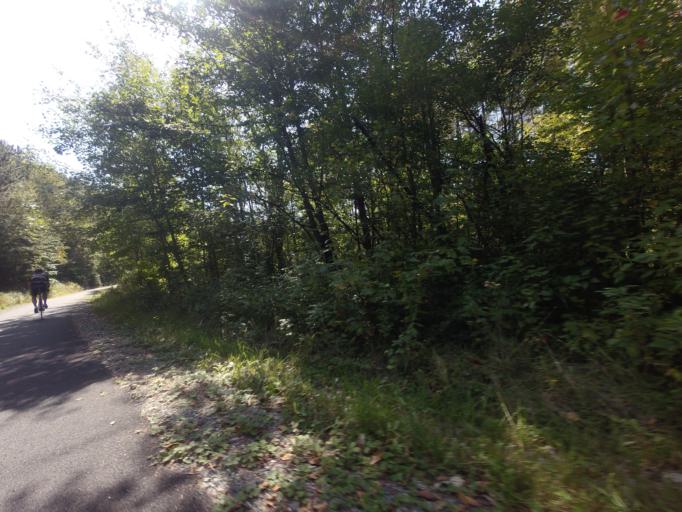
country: CA
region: Quebec
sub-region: Laurentides
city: Mont-Tremblant
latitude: 46.1148
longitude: -74.5010
